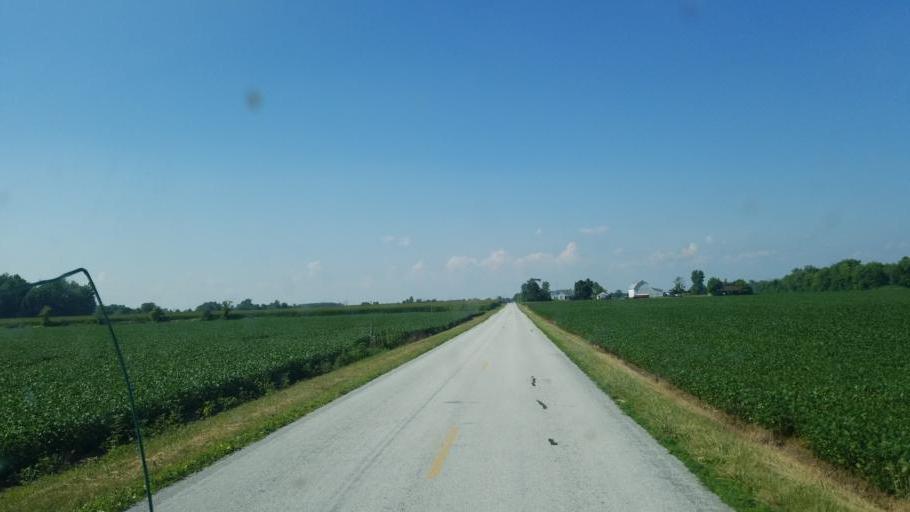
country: US
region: Ohio
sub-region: Hardin County
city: Forest
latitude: 40.6921
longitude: -83.4957
